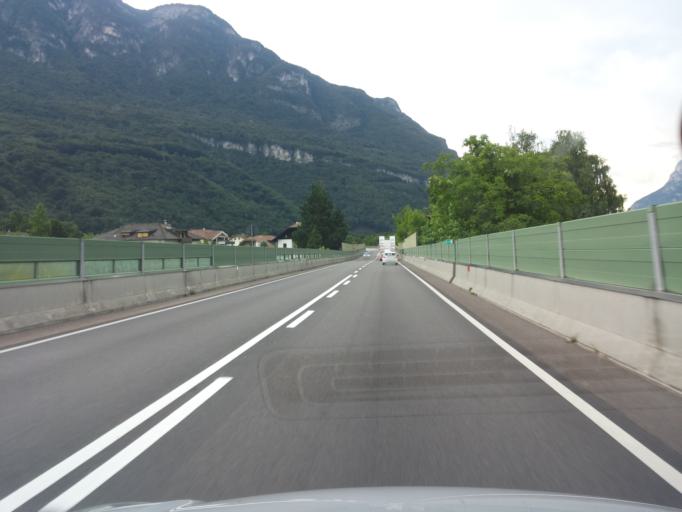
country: IT
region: Trentino-Alto Adige
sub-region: Bolzano
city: Egna
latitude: 46.3133
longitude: 11.2672
